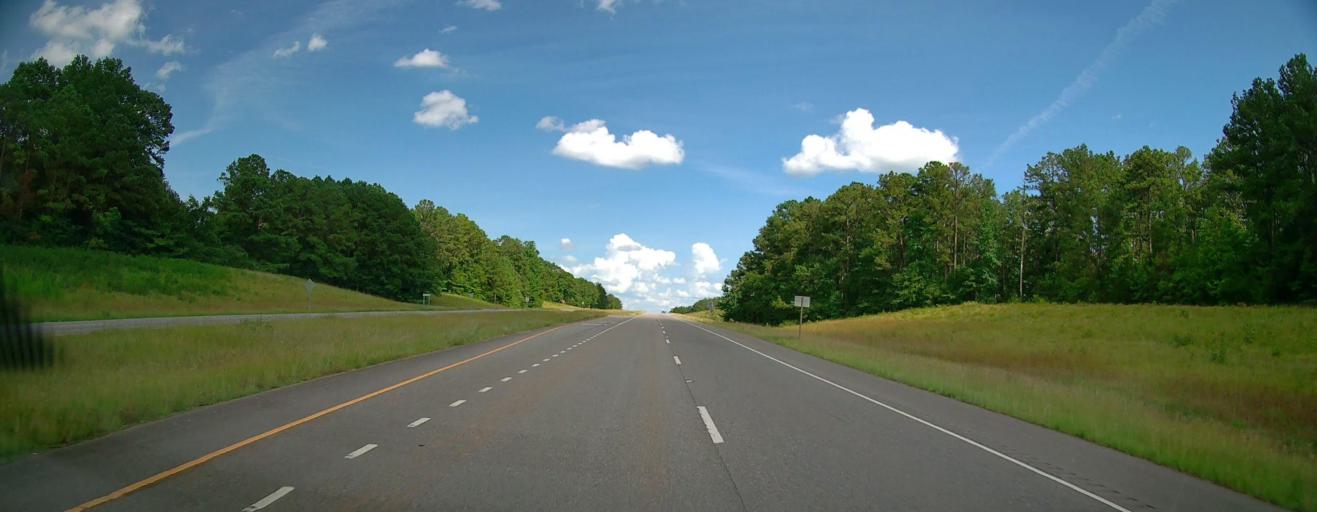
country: US
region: Alabama
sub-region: Pickens County
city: Reform
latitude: 33.3984
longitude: -88.0619
